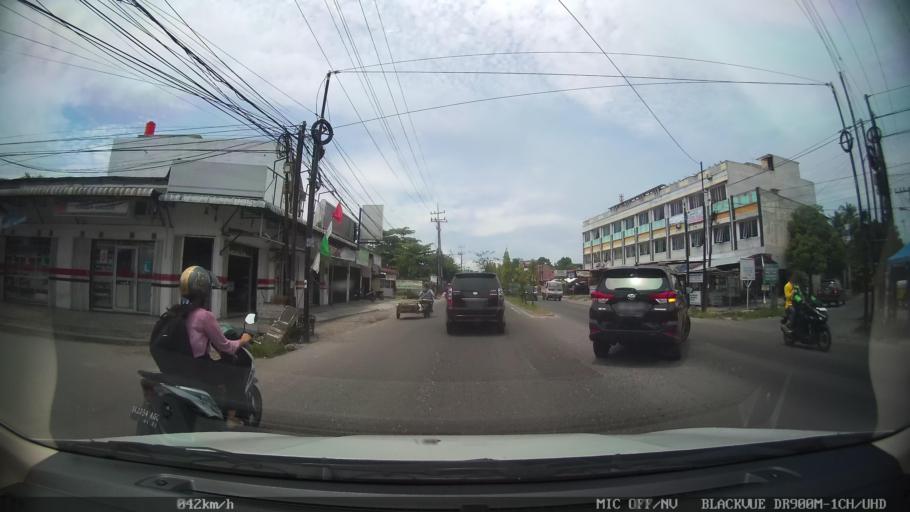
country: ID
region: North Sumatra
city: Sunggal
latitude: 3.5337
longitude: 98.6215
